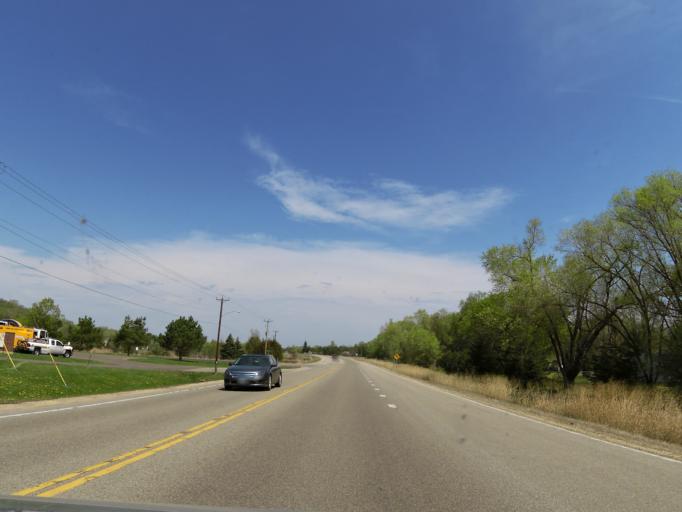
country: US
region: Minnesota
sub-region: Washington County
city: Lake Saint Croix Beach
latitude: 44.9263
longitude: -92.7718
